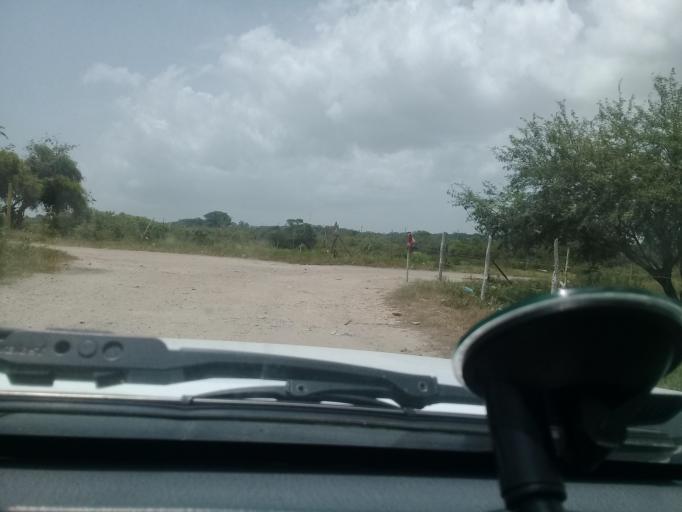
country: MX
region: Veracruz
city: Anahuac
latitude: 22.2232
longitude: -97.8244
